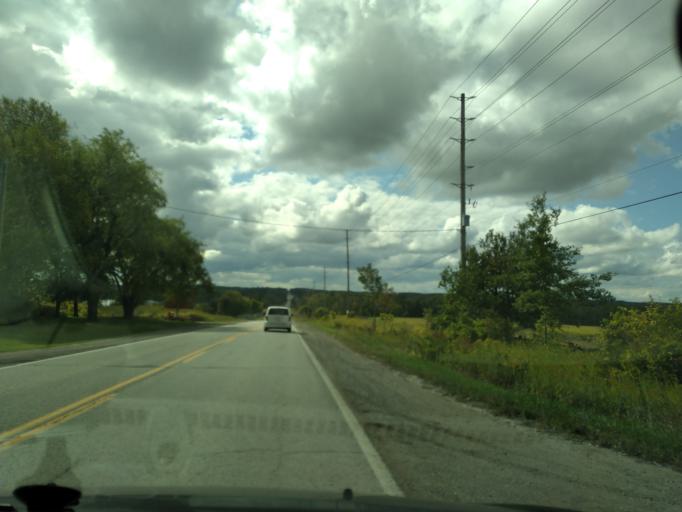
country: CA
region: Ontario
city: Innisfil
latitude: 44.2981
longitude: -79.6223
